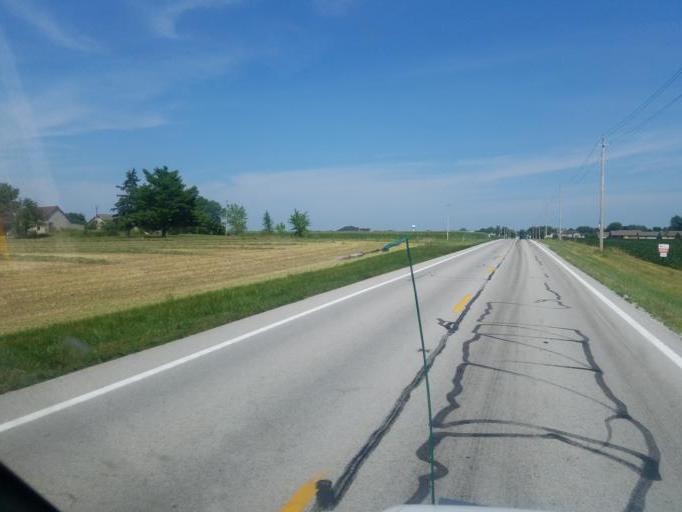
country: US
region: Ohio
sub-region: Auglaize County
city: Saint Marys
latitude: 40.4957
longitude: -84.3308
